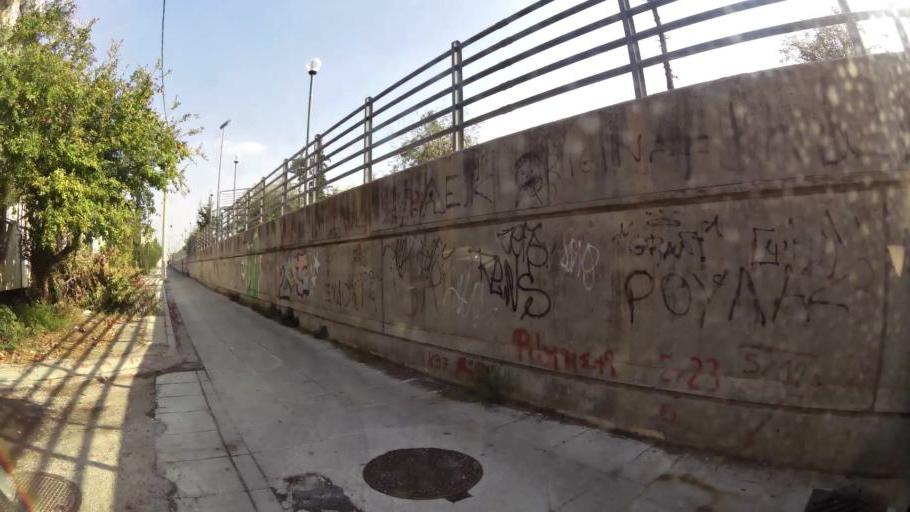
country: GR
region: Attica
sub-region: Nomarchia Dytikis Attikis
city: Zefyri
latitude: 38.0704
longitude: 23.7149
